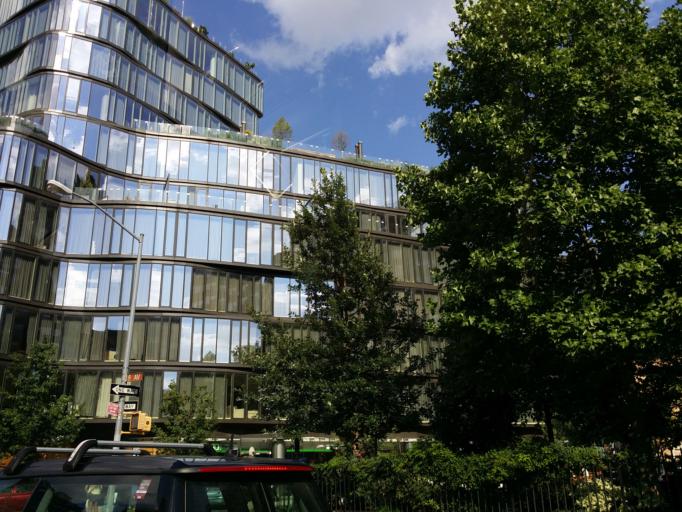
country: US
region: New York
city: New York City
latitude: 40.7390
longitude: -74.0029
